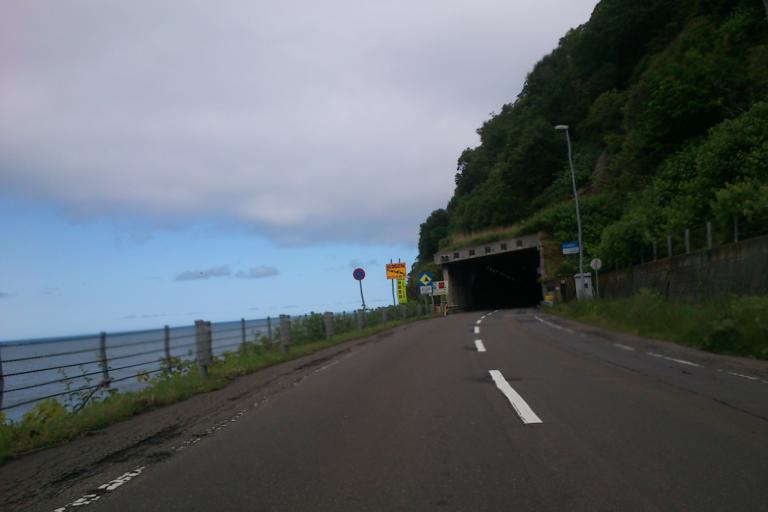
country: JP
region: Hokkaido
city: Ishikari
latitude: 43.4372
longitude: 141.4169
